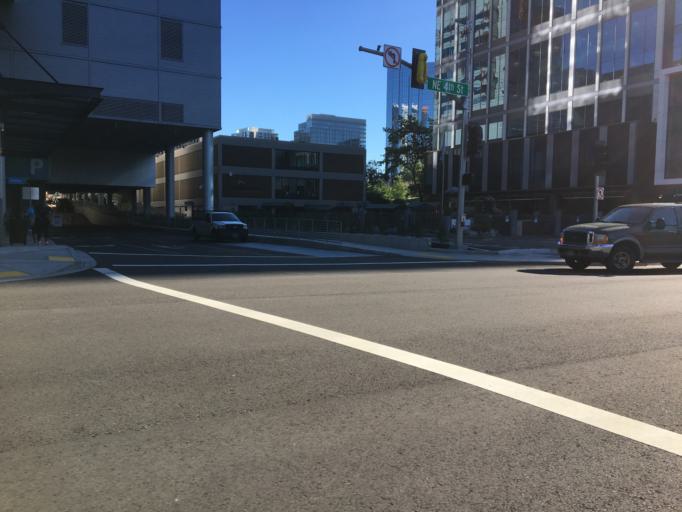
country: US
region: Washington
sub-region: King County
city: Bellevue
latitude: 47.6139
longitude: -122.2006
